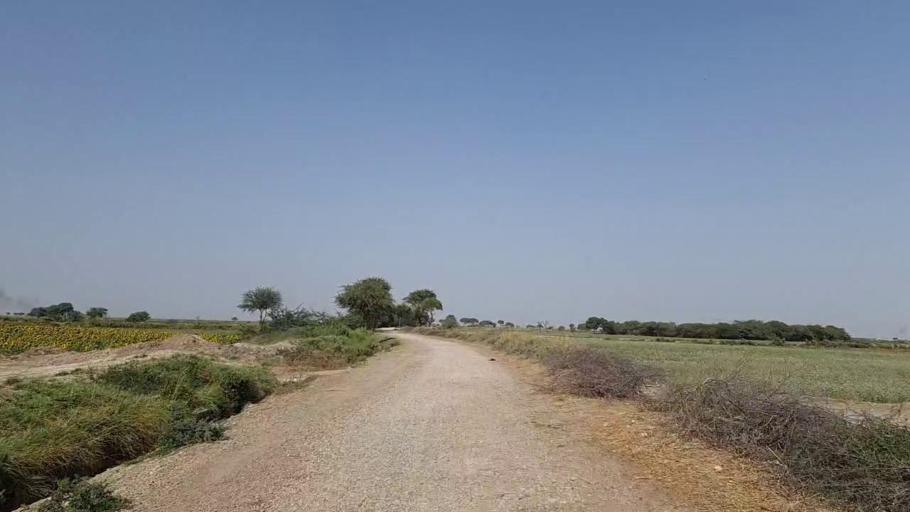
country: PK
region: Sindh
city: Jati
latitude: 24.3456
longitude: 68.3059
